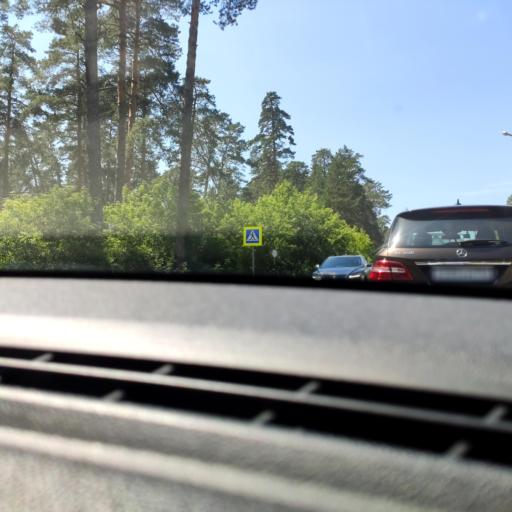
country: RU
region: Samara
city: Tol'yatti
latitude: 53.4753
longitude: 49.3446
